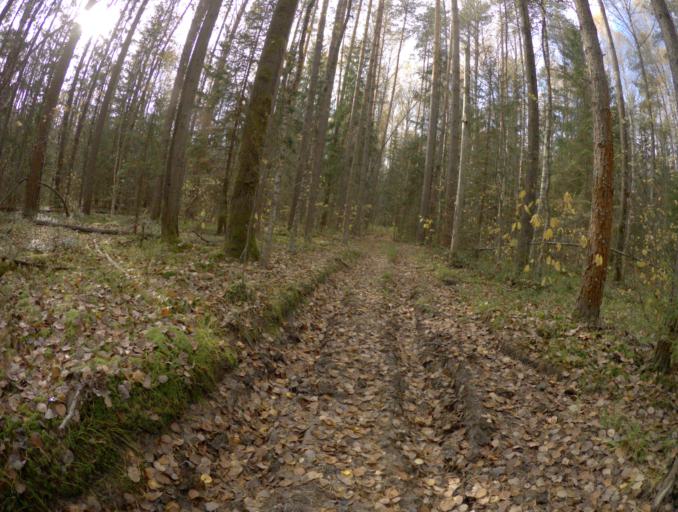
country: RU
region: Vladimir
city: Raduzhnyy
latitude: 55.9649
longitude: 40.3588
